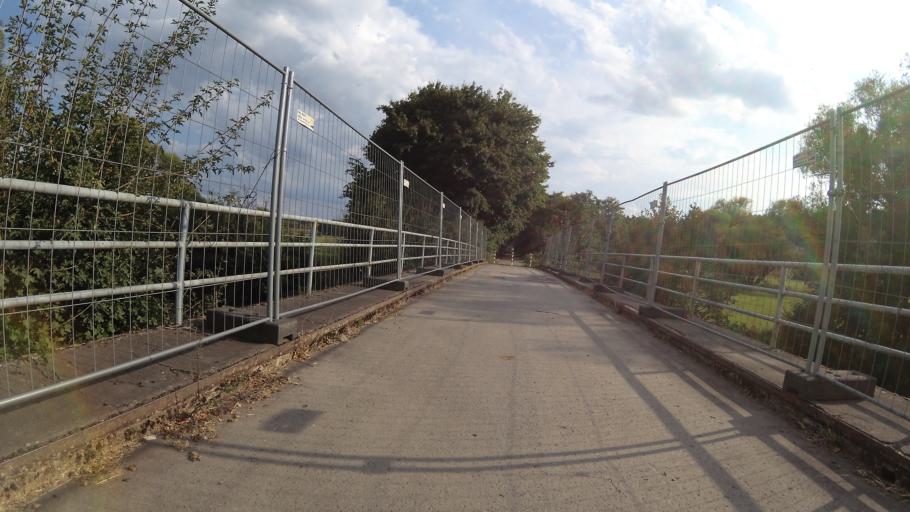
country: DE
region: Saarland
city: Bexbach
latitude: 49.3267
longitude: 7.2602
